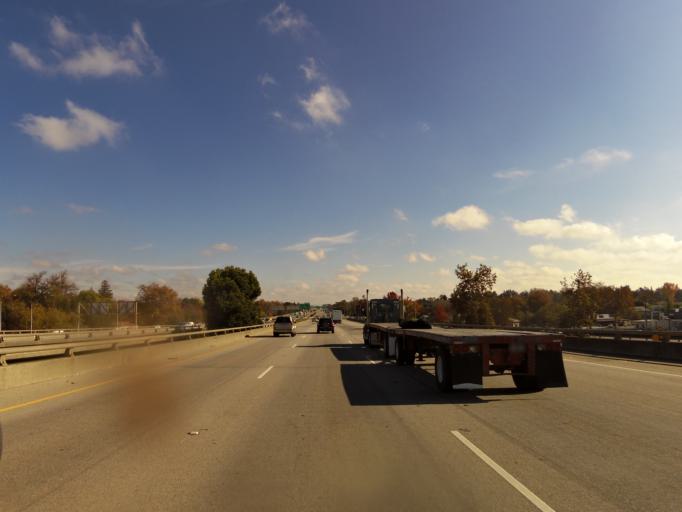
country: US
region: California
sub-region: Sacramento County
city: Sacramento
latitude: 38.5676
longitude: -121.5093
